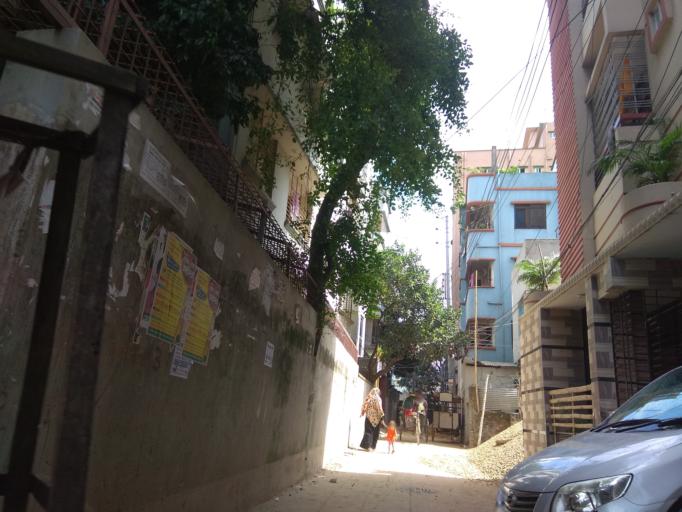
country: BD
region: Dhaka
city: Tungi
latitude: 23.8145
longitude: 90.3923
